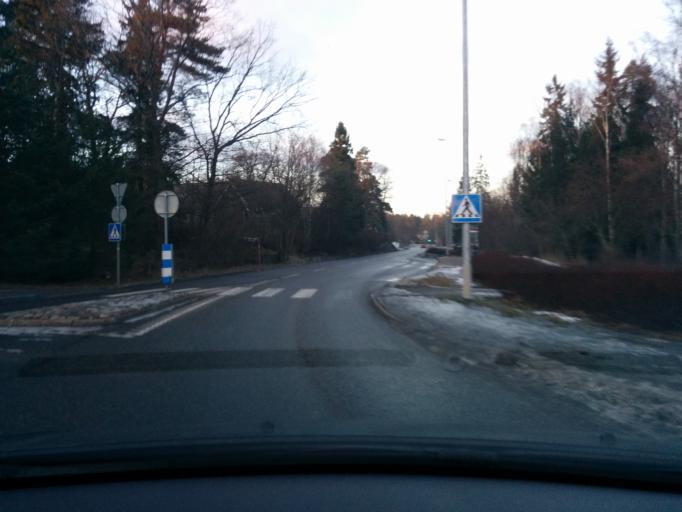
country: SE
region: Stockholm
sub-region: Nacka Kommun
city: Alta
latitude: 59.2681
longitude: 18.1771
